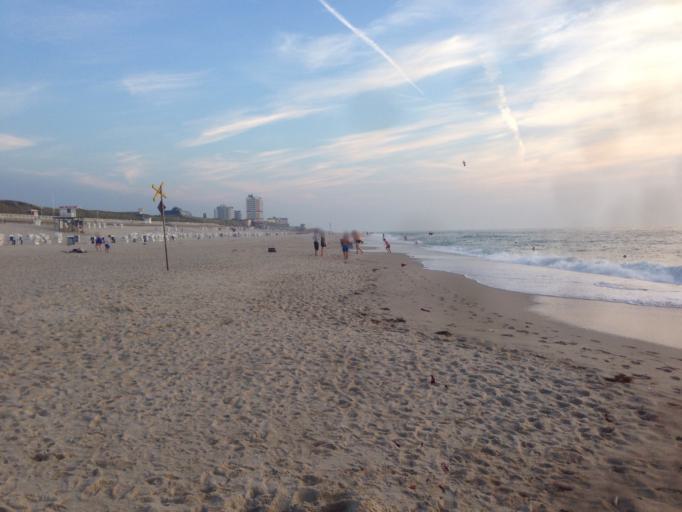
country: DE
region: Schleswig-Holstein
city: Westerland
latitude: 54.9166
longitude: 8.3018
